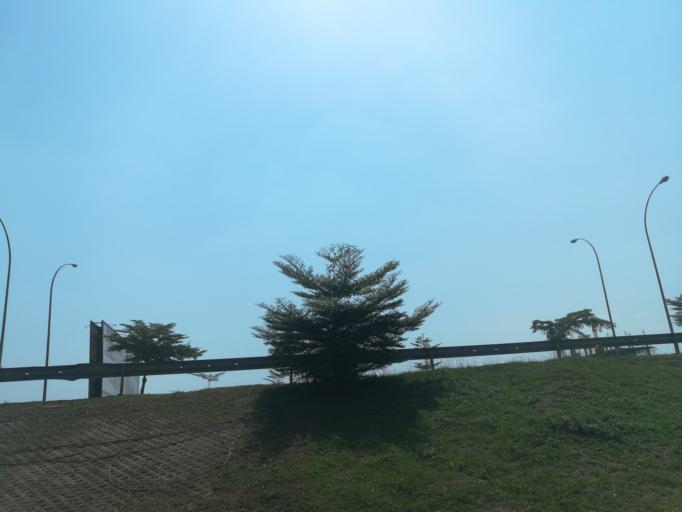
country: NG
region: Abuja Federal Capital Territory
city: Abuja
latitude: 9.0788
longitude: 7.4295
